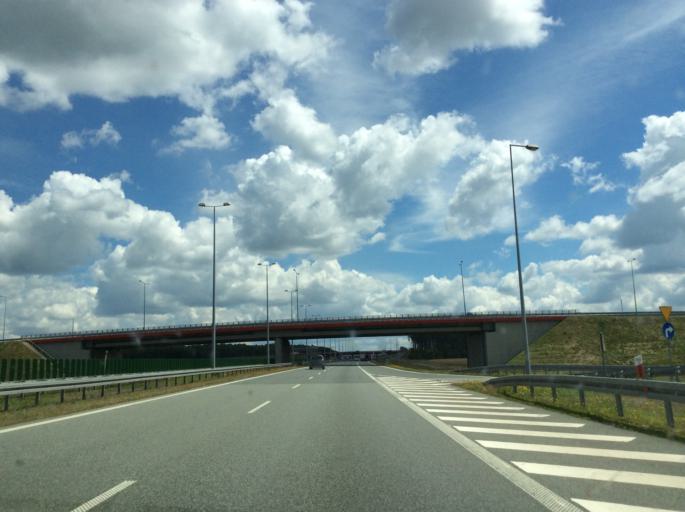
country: PL
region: Greater Poland Voivodeship
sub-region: Powiat koninski
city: Stare Miasto
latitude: 52.1563
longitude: 18.2647
